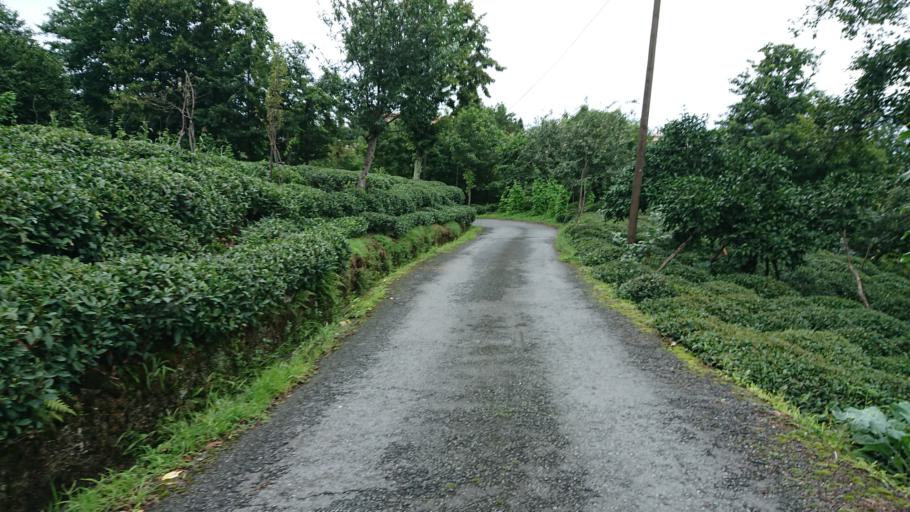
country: TR
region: Rize
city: Rize
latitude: 40.9824
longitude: 40.4855
